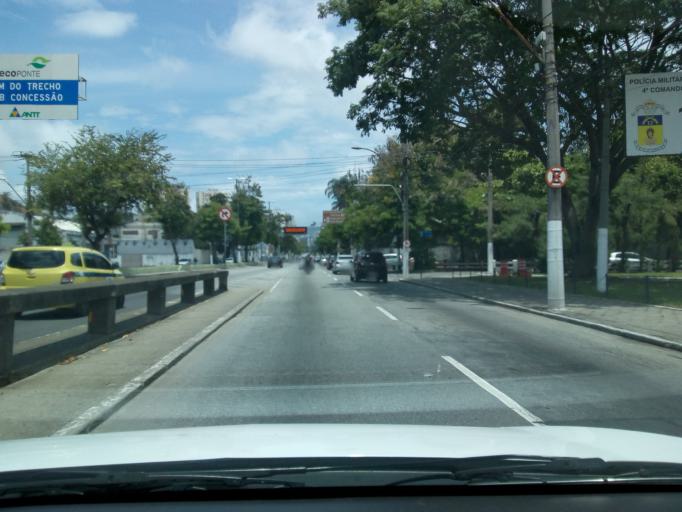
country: BR
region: Rio de Janeiro
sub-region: Niteroi
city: Niteroi
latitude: -22.8853
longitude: -43.1155
